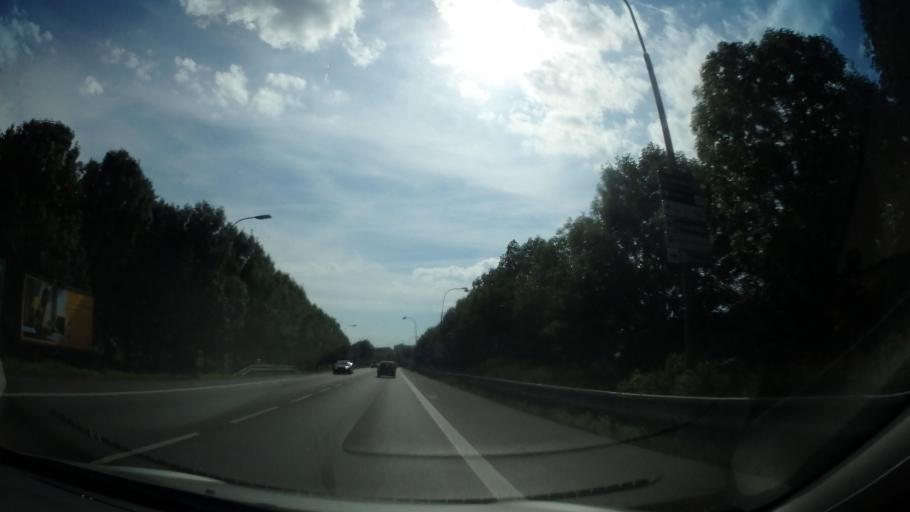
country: CZ
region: Jihocesky
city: Strakonice
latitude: 49.2621
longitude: 13.9149
